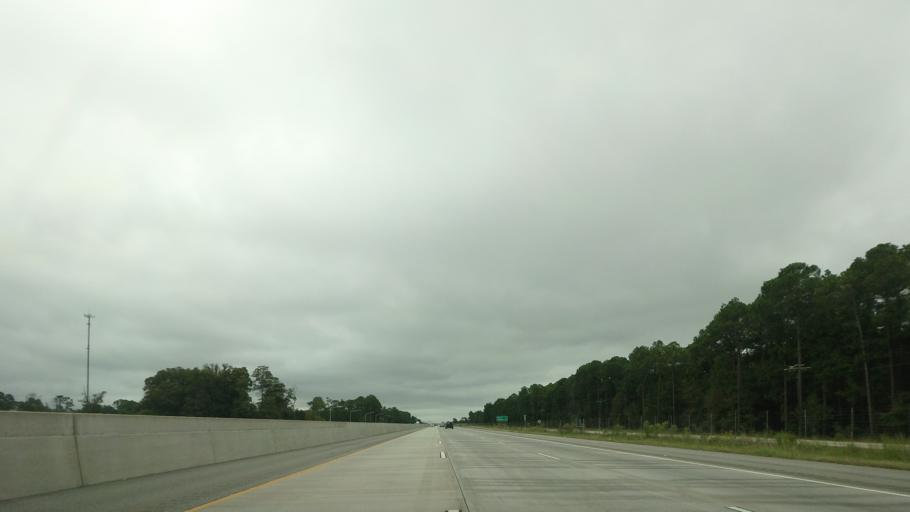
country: US
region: Georgia
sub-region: Cook County
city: Sparks
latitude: 31.2483
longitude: -83.4675
